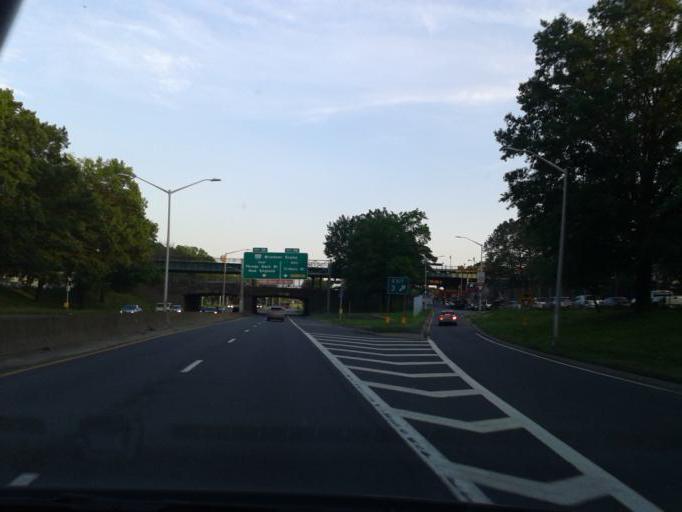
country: US
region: New York
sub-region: Bronx
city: The Bronx
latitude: 40.8313
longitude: -73.8739
